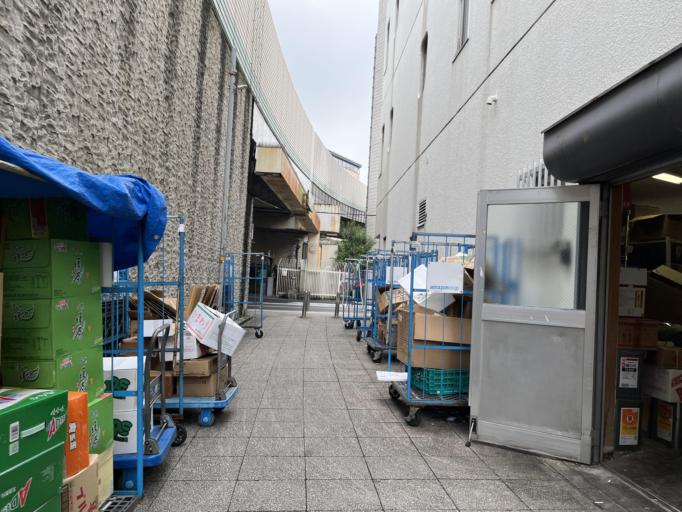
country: JP
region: Kanagawa
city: Yokohama
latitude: 35.4402
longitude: 139.6418
